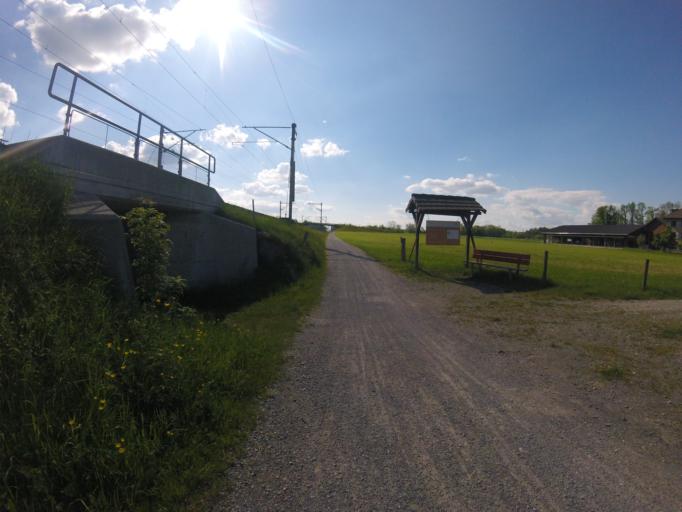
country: CH
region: Saint Gallen
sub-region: Wahlkreis St. Gallen
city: Gossau
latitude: 47.4059
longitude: 9.2254
